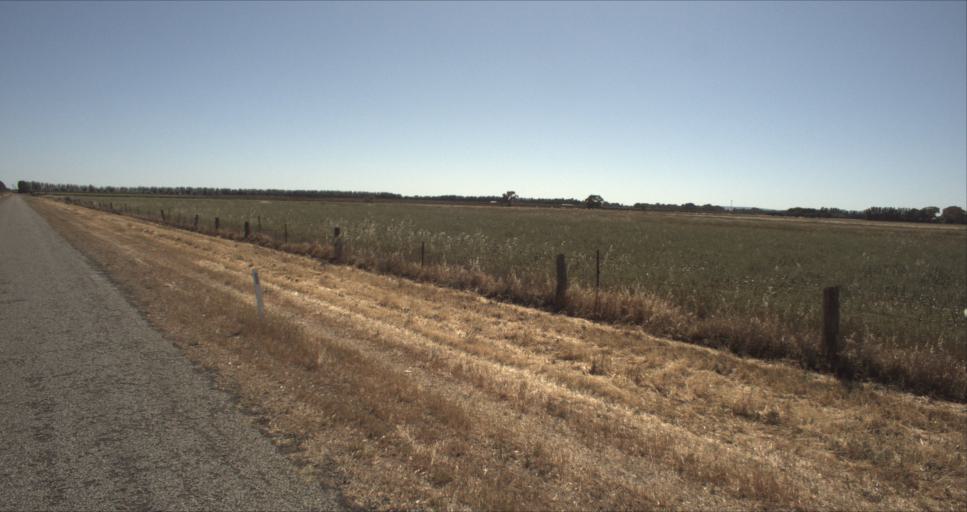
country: AU
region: New South Wales
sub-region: Leeton
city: Leeton
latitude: -34.5361
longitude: 146.3174
